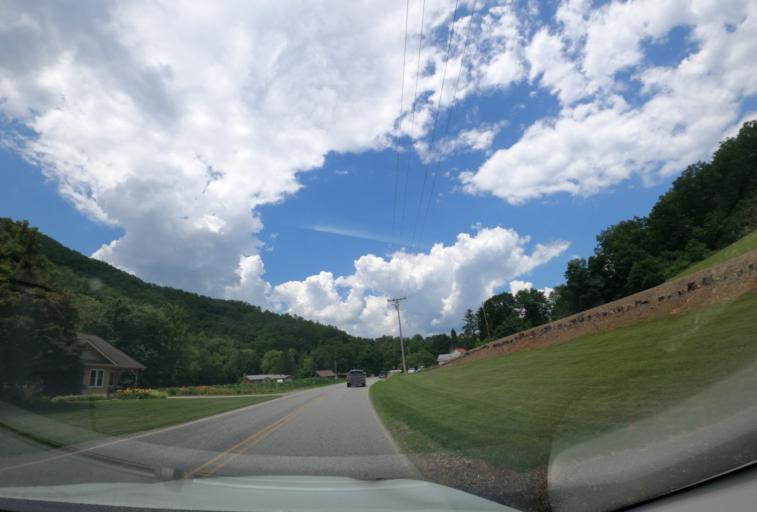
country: US
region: North Carolina
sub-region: Haywood County
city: Waynesville
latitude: 35.4421
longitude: -82.9177
